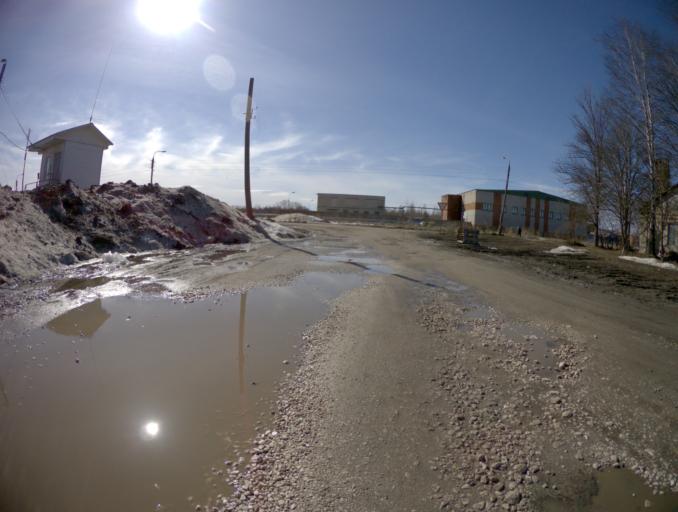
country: RU
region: Vladimir
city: Suzdal'
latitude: 56.4426
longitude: 40.4543
